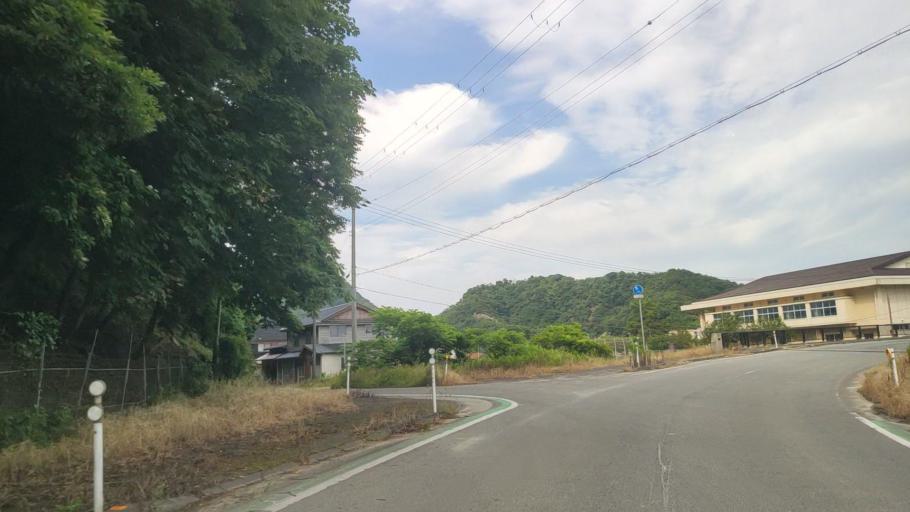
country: JP
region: Hyogo
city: Toyooka
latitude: 35.6412
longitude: 134.8409
